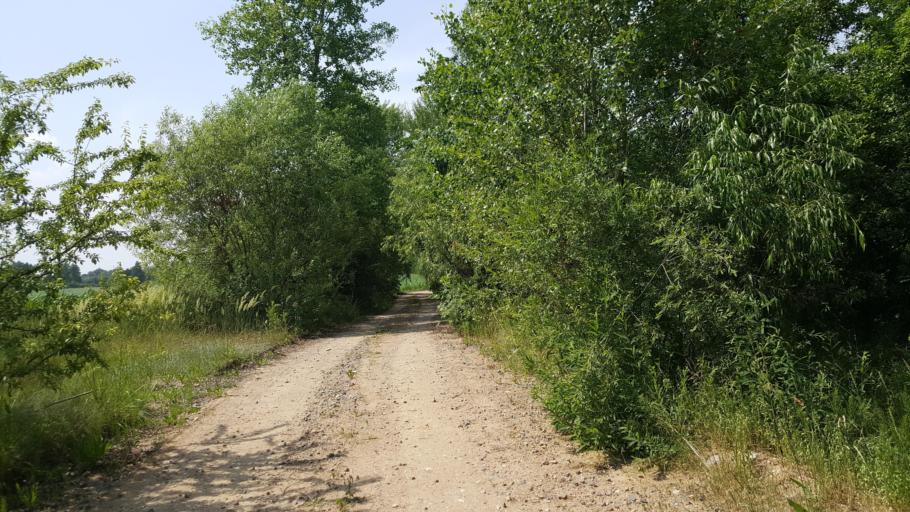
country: BY
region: Brest
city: Kamyanyets
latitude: 52.3650
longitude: 23.7599
